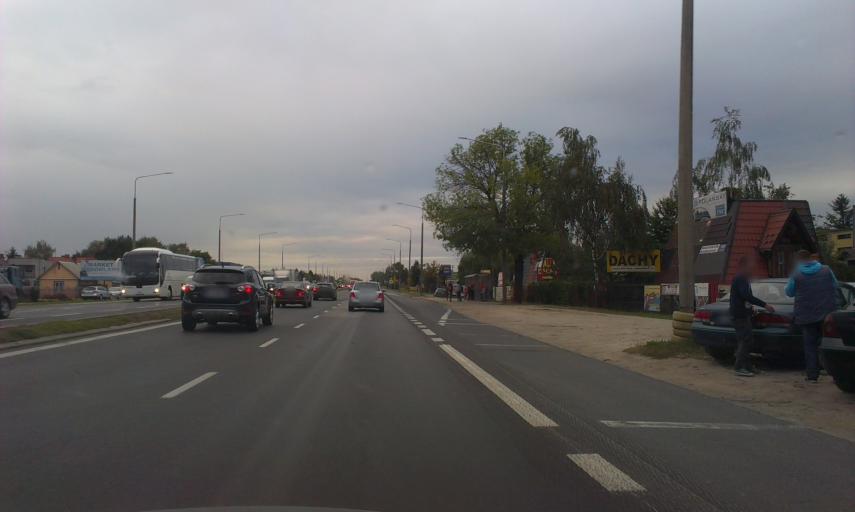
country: PL
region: Masovian Voivodeship
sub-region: Radom
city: Radom
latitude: 51.4429
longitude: 21.1454
